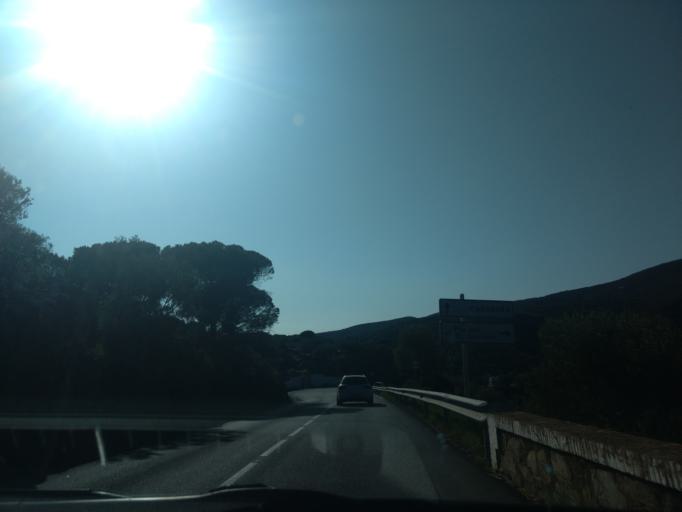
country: ES
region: Catalonia
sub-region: Provincia de Girona
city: Cadaques
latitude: 42.2919
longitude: 3.2702
